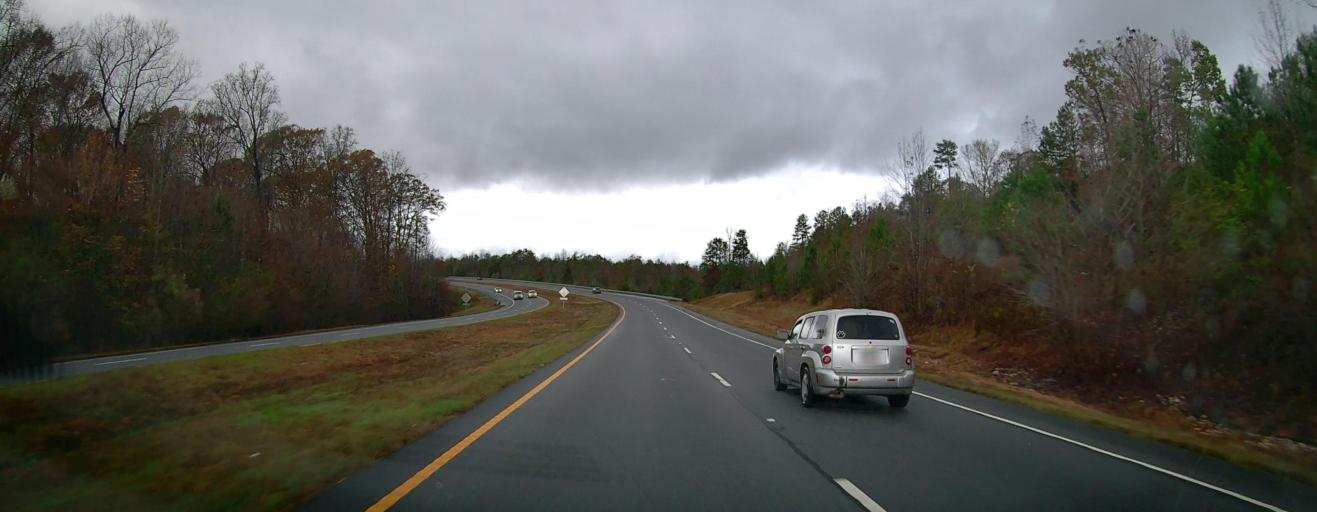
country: US
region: Georgia
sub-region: Jackson County
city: Nicholson
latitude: 34.0572
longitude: -83.4117
